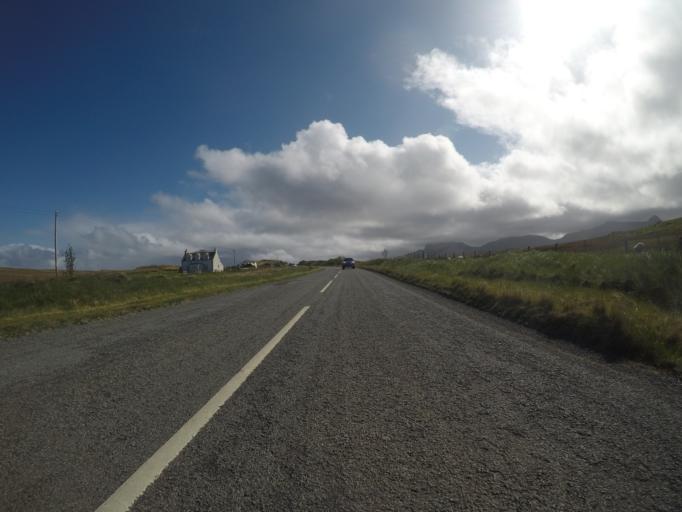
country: GB
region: Scotland
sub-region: Highland
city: Portree
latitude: 57.5749
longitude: -6.1548
